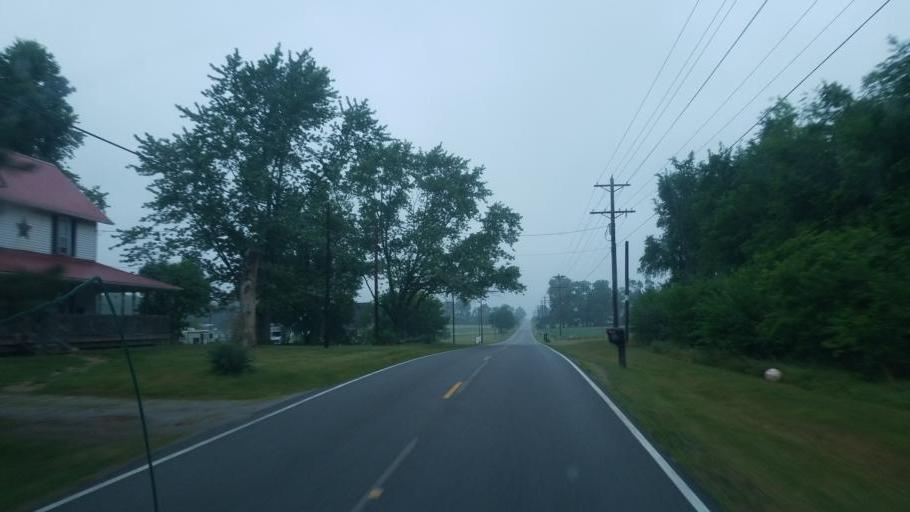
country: US
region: Ohio
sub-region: Defiance County
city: Hicksville
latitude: 41.3420
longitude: -84.7092
